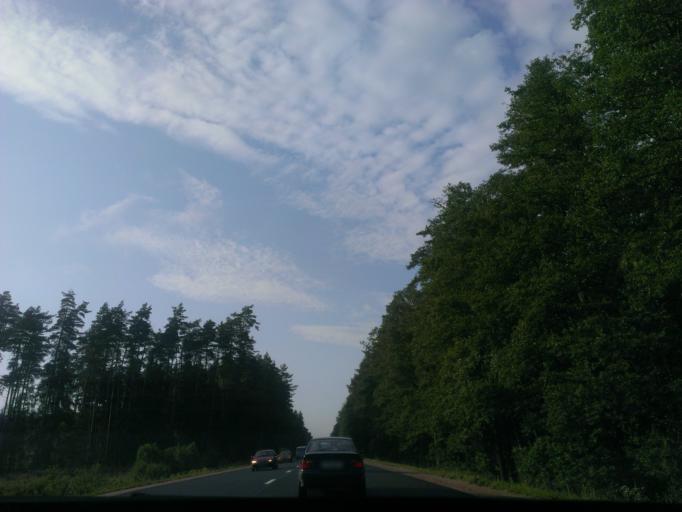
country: LV
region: Kekava
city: Kekava
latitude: 56.7438
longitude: 24.2511
